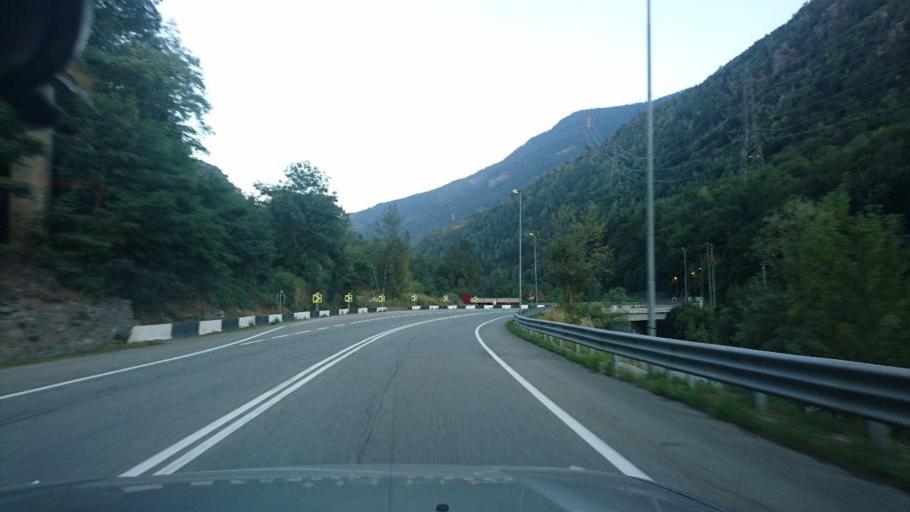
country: IT
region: Aosta Valley
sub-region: Valle d'Aosta
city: Avise
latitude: 45.7167
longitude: 7.1104
